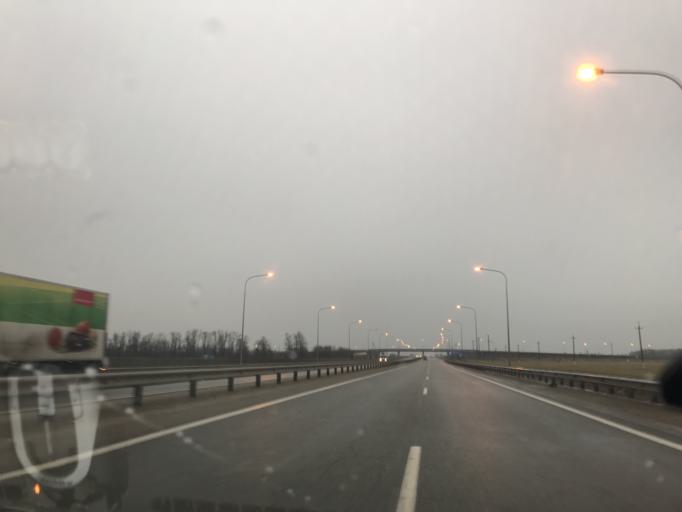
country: RU
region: Krasnodarskiy
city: Pavlovskaya
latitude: 46.2476
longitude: 39.8316
